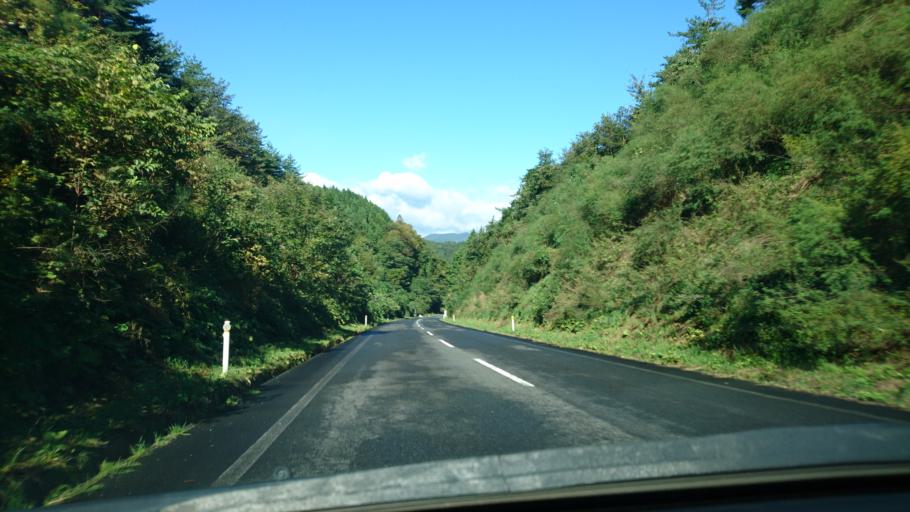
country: JP
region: Iwate
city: Ichinoseki
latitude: 39.0064
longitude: 141.0323
